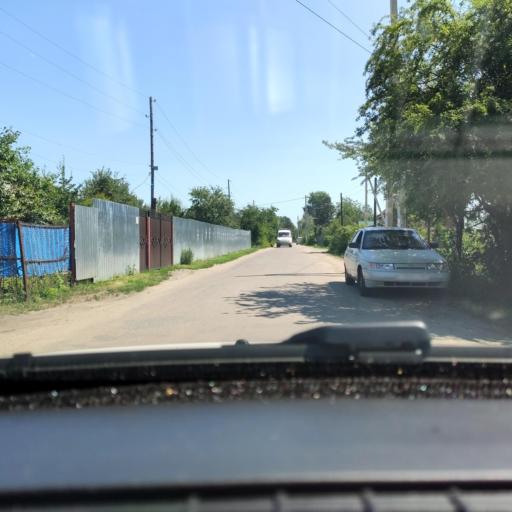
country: RU
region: Voronezj
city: Shilovo
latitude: 51.5869
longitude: 39.1563
